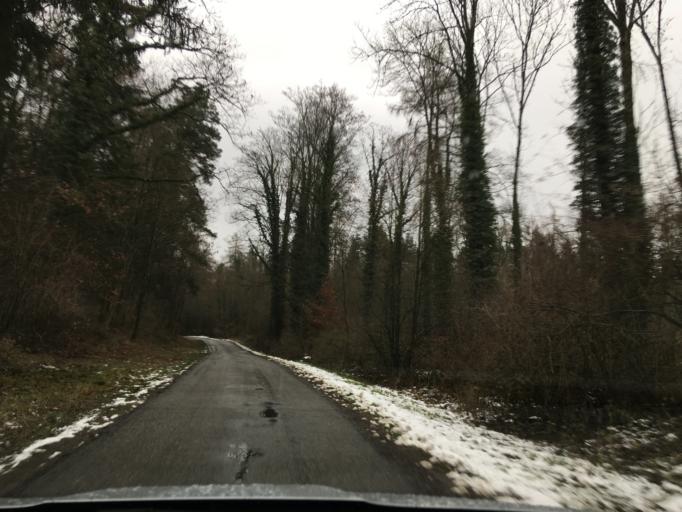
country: DE
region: Baden-Wuerttemberg
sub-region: Freiburg Region
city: Hilzingen
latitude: 47.7473
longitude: 8.8016
